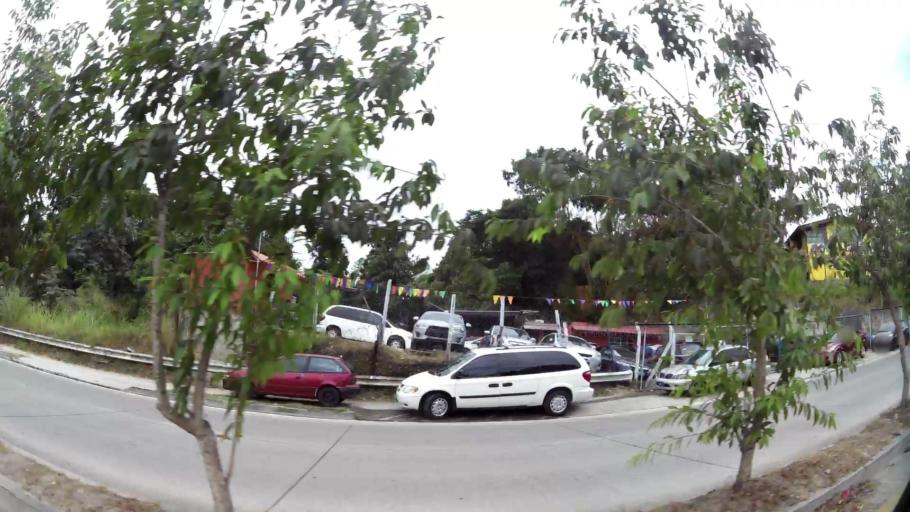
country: SV
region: San Salvador
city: Mejicanos
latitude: 13.7216
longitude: -89.2324
